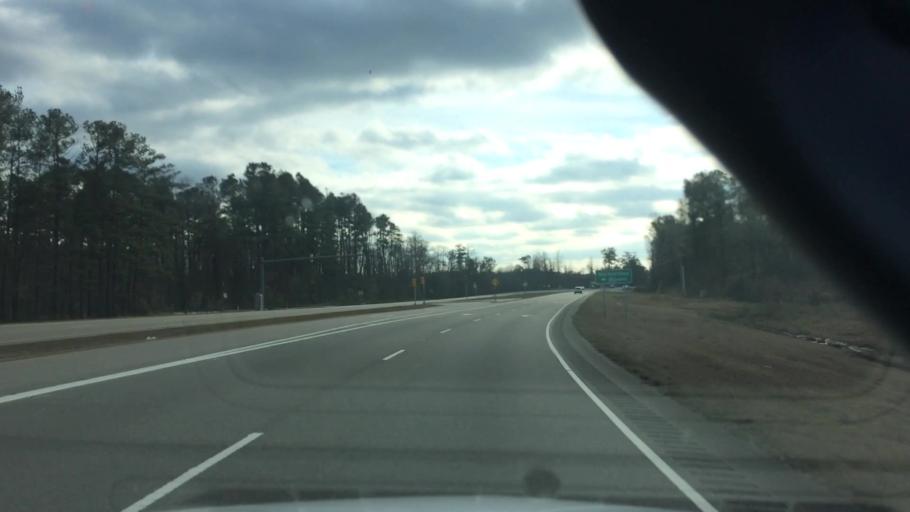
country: US
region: North Carolina
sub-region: Brunswick County
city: Bolivia
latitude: 34.1381
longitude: -78.0936
